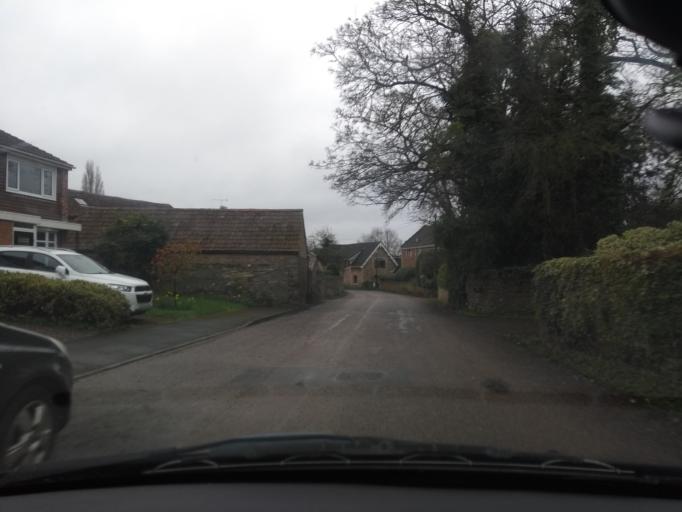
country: GB
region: England
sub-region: Somerset
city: Taunton
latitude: 51.0329
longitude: -3.1247
